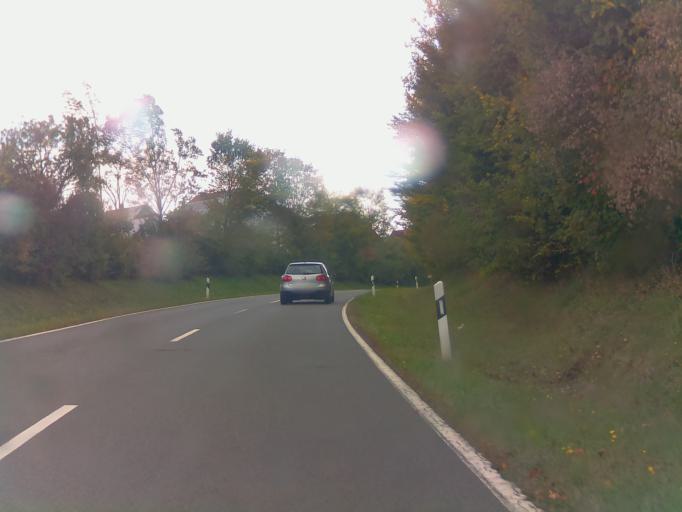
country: DE
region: Baden-Wuerttemberg
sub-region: Regierungsbezirk Stuttgart
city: Grossrinderfeld
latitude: 49.6662
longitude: 9.7445
